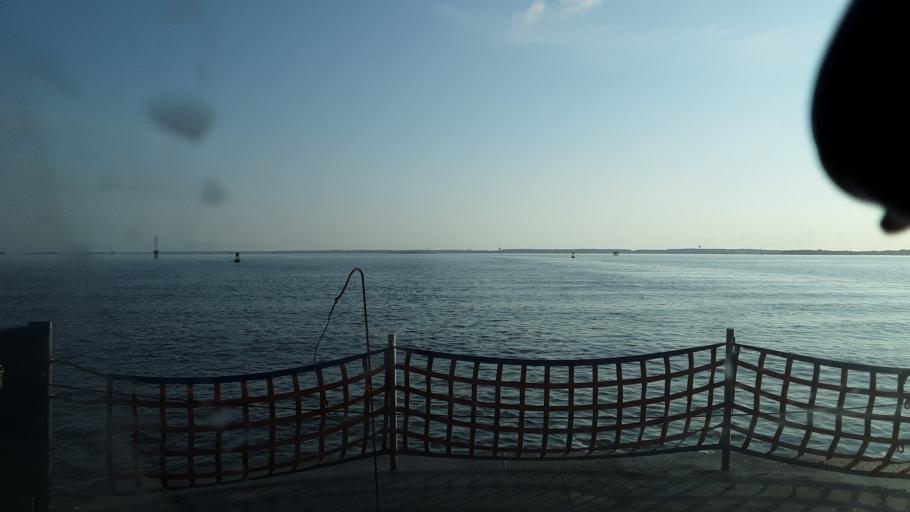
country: US
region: North Carolina
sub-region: New Hanover County
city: Kure Beach
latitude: 33.9567
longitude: -77.9572
